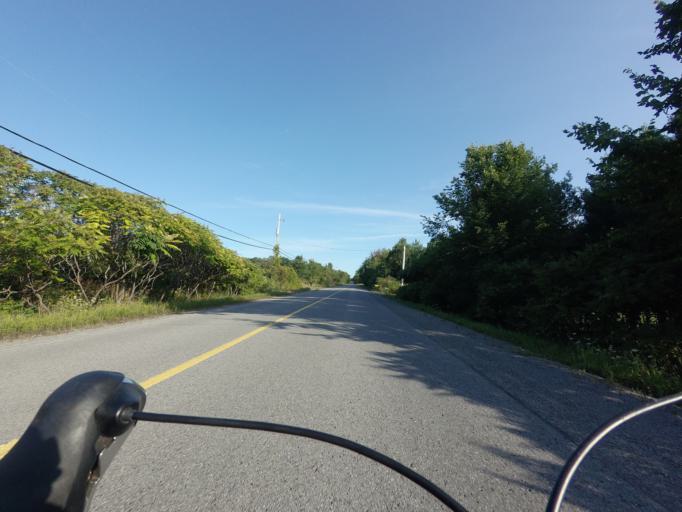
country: CA
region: Ontario
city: Bells Corners
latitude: 45.4342
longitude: -75.9883
